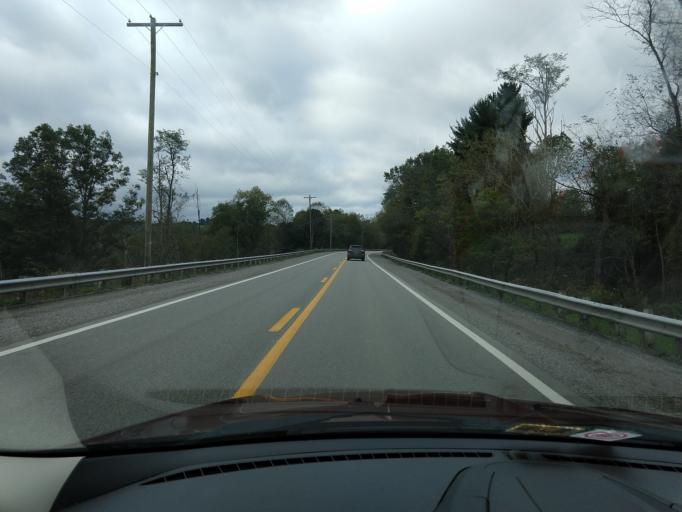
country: US
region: West Virginia
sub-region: Barbour County
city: Belington
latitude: 39.0328
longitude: -79.9485
